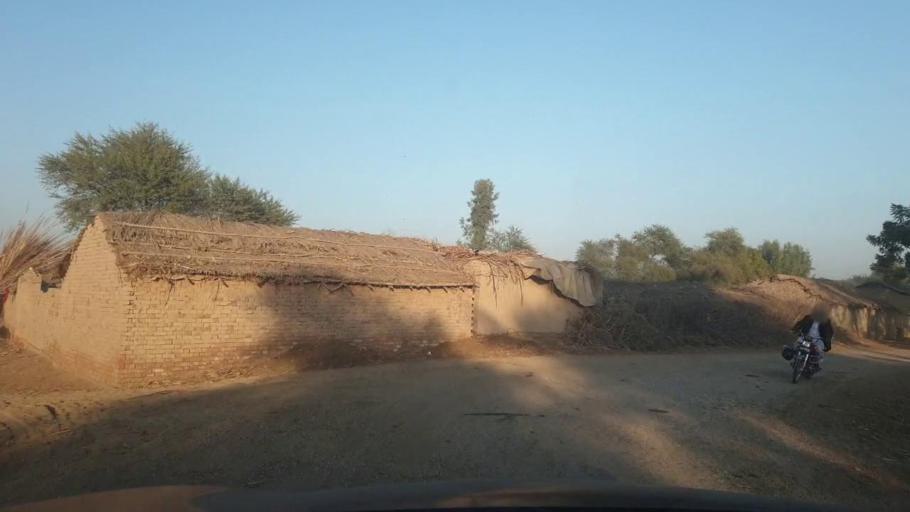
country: PK
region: Sindh
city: Ubauro
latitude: 28.1697
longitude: 69.5802
